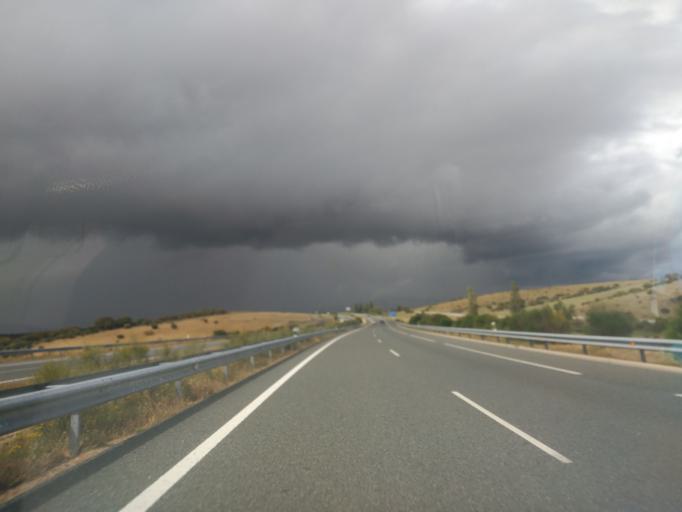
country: ES
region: Castille and Leon
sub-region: Provincia de Salamanca
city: Belena
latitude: 40.7565
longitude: -5.6319
